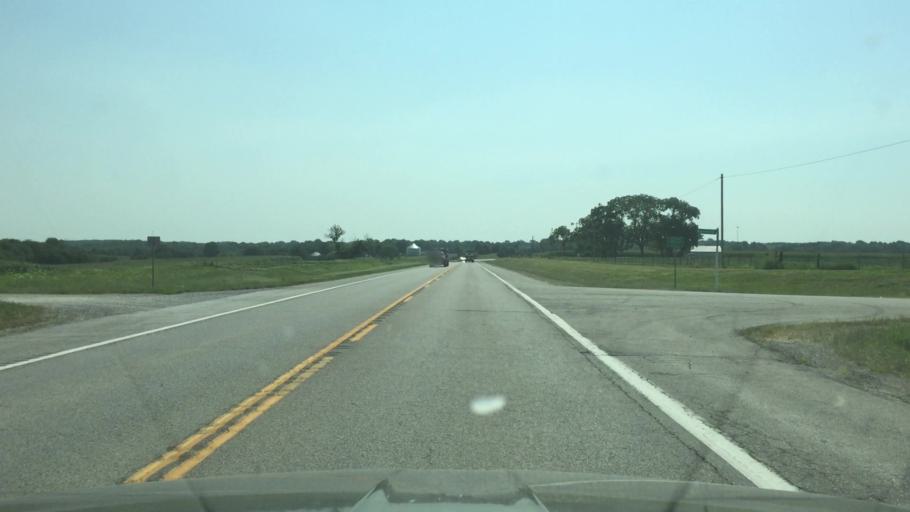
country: US
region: Missouri
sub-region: Pettis County
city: Sedalia
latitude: 38.6916
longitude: -93.0604
